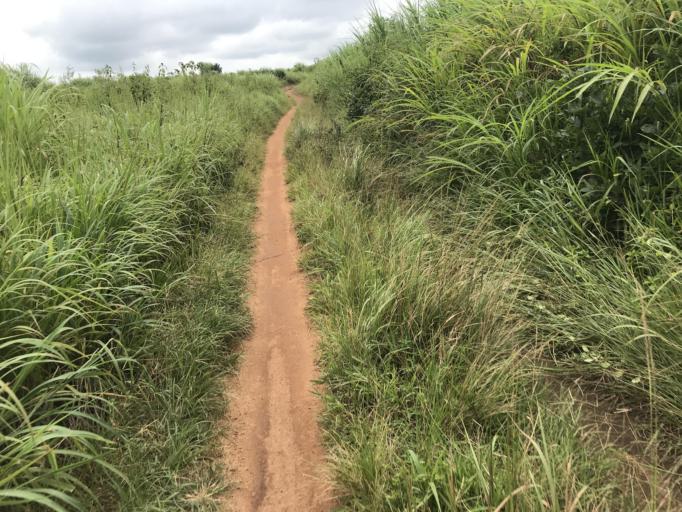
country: SL
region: Eastern Province
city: Buedu
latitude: 8.4709
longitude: -10.3231
